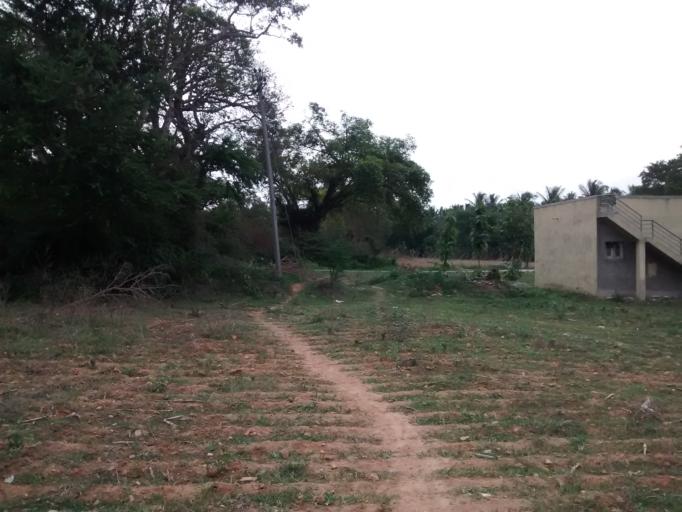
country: IN
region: Karnataka
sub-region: Hassan
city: Hassan
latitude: 12.9468
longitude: 76.1661
